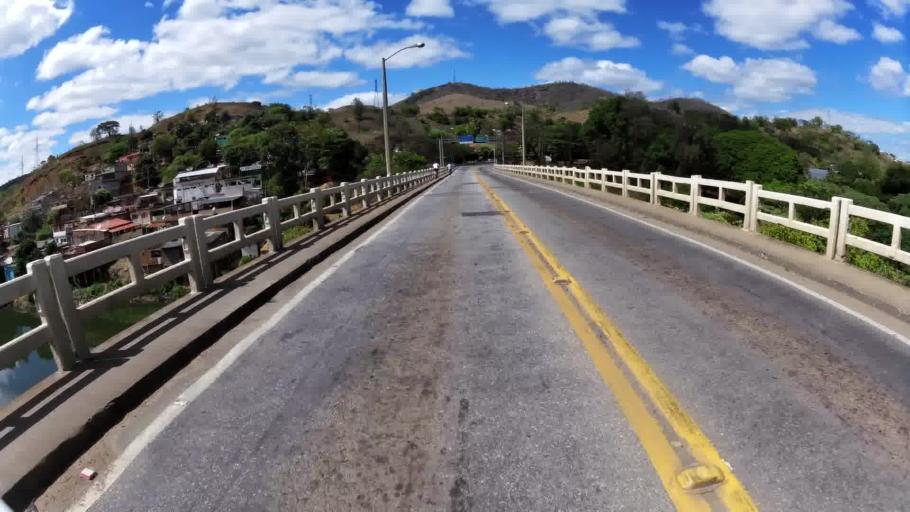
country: BR
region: Minas Gerais
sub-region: Alem Paraiba
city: Alem Paraiba
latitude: -21.8745
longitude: -42.6675
